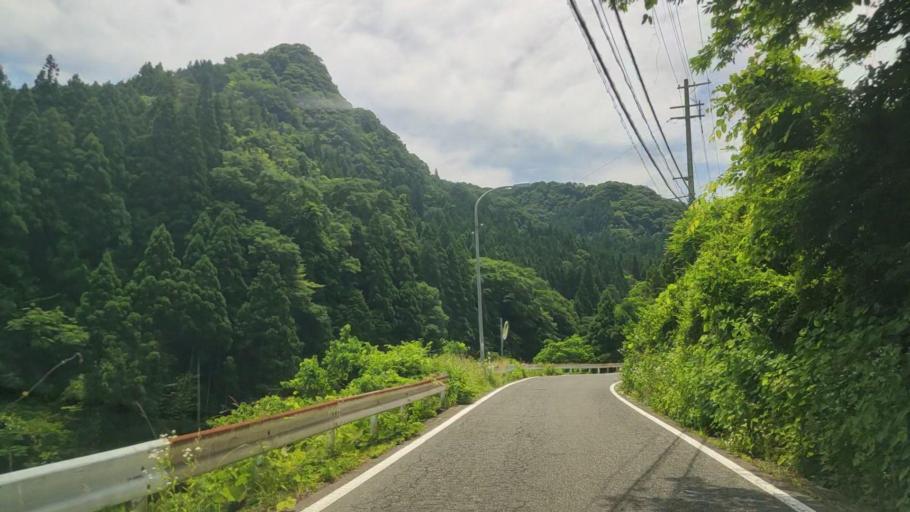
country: JP
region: Tottori
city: Tottori
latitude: 35.4368
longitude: 134.5325
